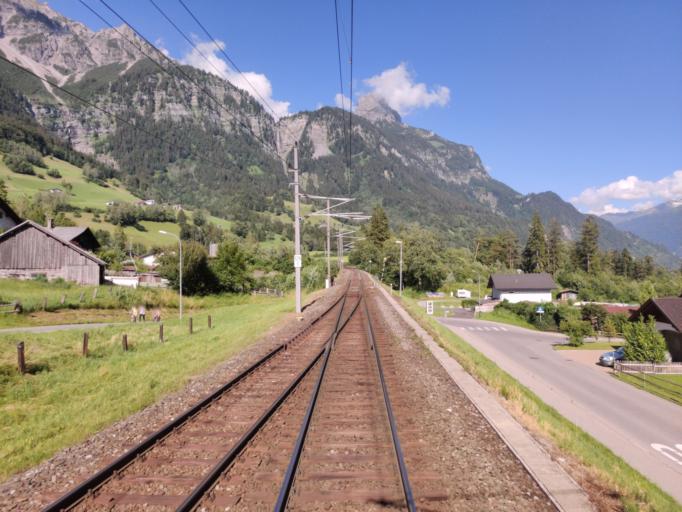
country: AT
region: Vorarlberg
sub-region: Politischer Bezirk Bludenz
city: Innerbraz
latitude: 47.1484
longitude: 9.9006
